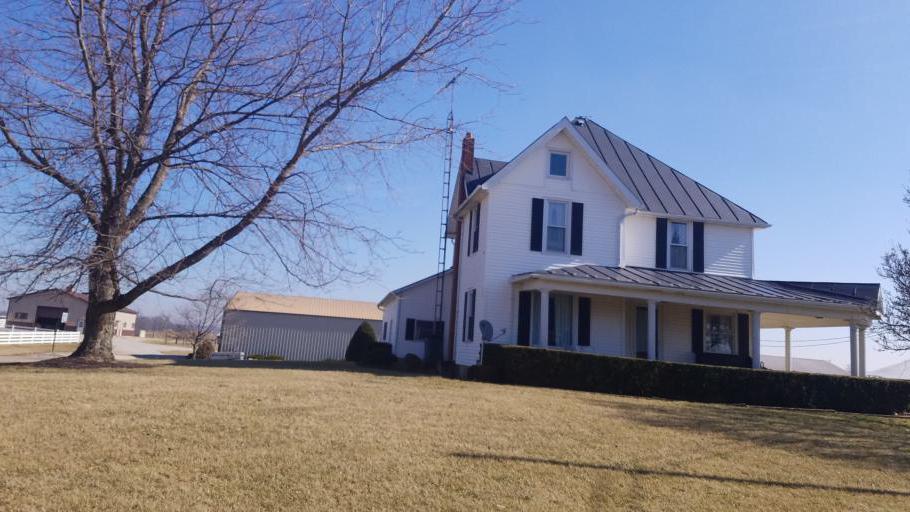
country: US
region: Ohio
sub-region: Richland County
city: Shelby
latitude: 40.8901
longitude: -82.5542
